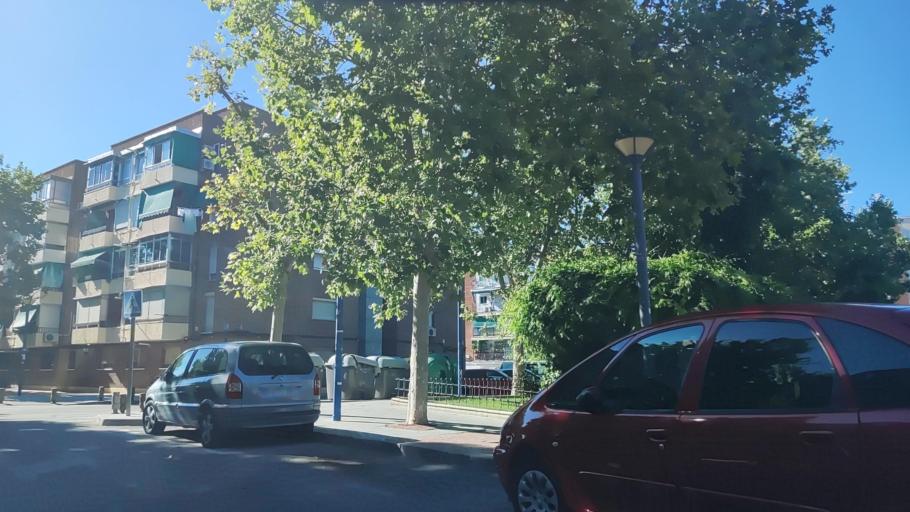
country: ES
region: Madrid
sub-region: Provincia de Madrid
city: Leganes
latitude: 40.3332
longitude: -3.7629
